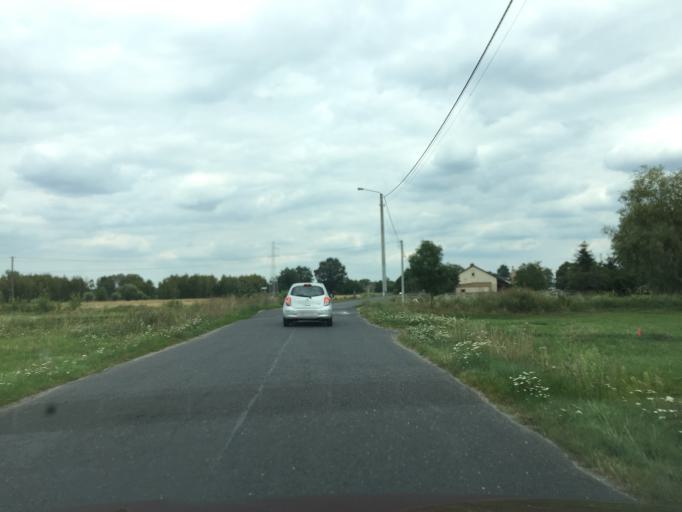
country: PL
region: Greater Poland Voivodeship
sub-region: Powiat kaliski
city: Stawiszyn
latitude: 51.9524
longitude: 18.1683
